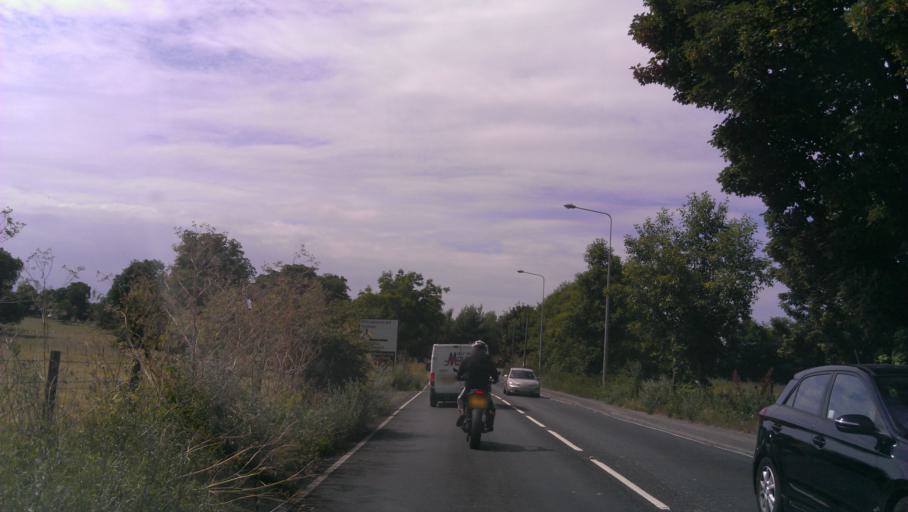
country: GB
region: England
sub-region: Kent
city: Faversham
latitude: 51.3131
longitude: 0.8669
